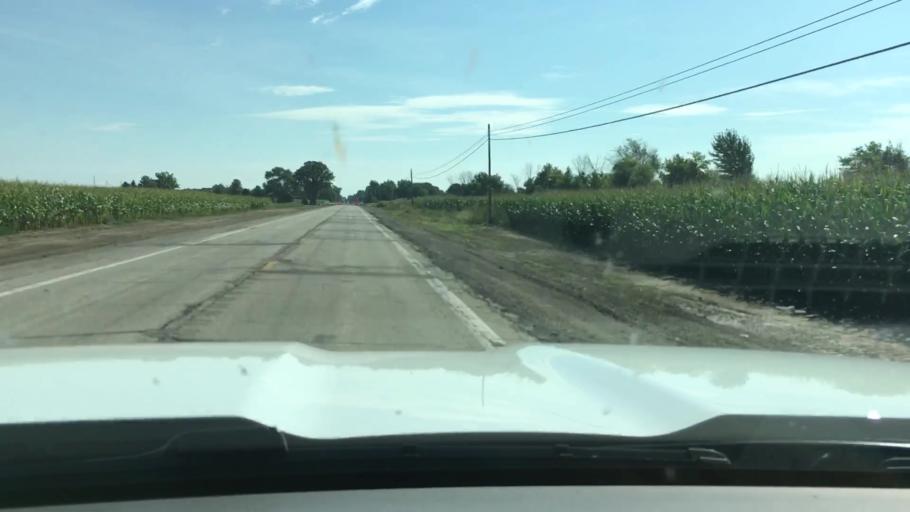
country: US
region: Michigan
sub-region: Saginaw County
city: Hemlock
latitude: 43.4122
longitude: -84.2810
